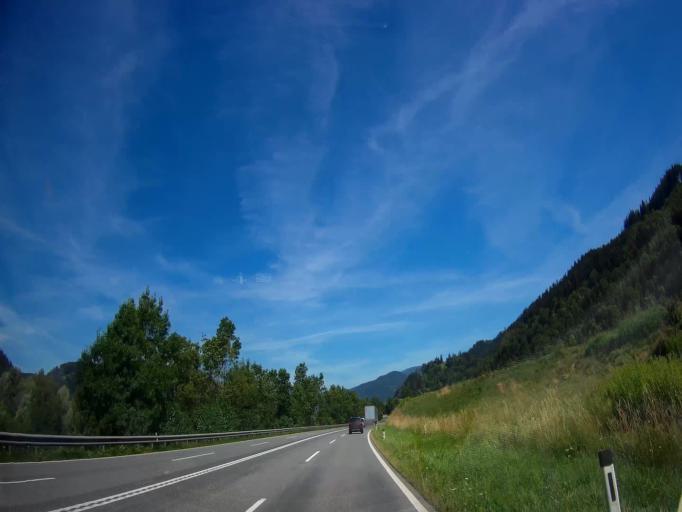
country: AT
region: Carinthia
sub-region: Politischer Bezirk Sankt Veit an der Glan
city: Micheldorf
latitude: 46.9084
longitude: 14.4373
